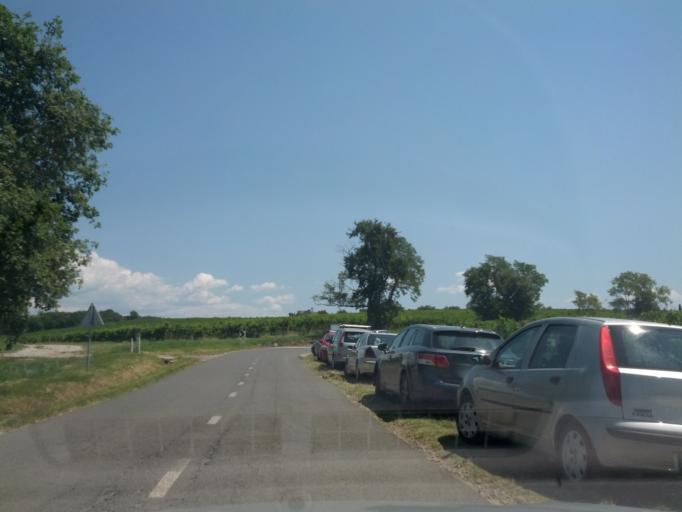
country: SI
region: Koper-Capodistria
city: Ankaran
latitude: 45.5880
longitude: 13.7131
